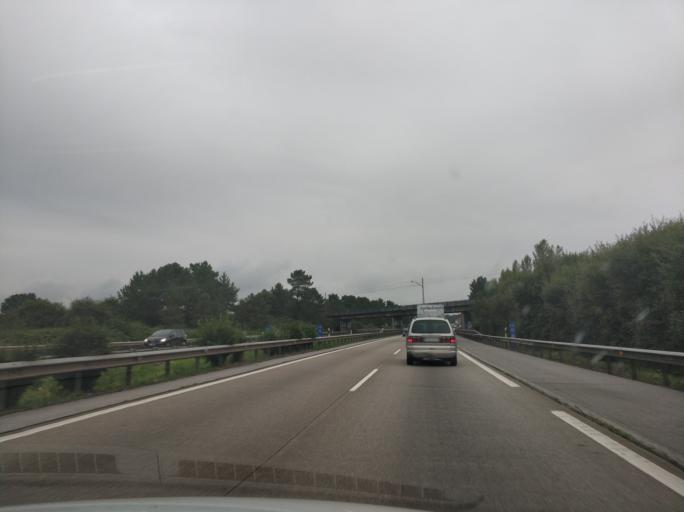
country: ES
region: Asturias
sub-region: Province of Asturias
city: Lugones
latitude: 43.4286
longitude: -5.8022
